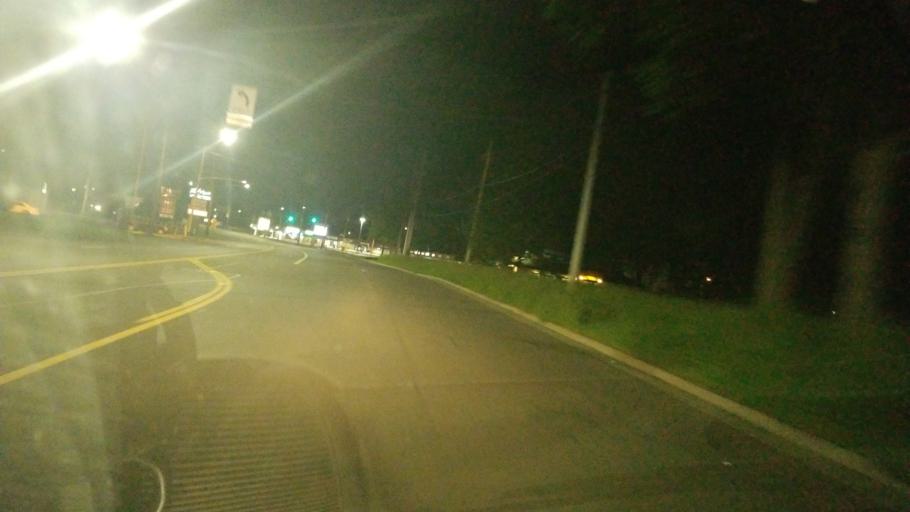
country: US
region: Ohio
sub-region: Trumbull County
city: McKinley Heights
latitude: 41.1958
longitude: -80.7278
